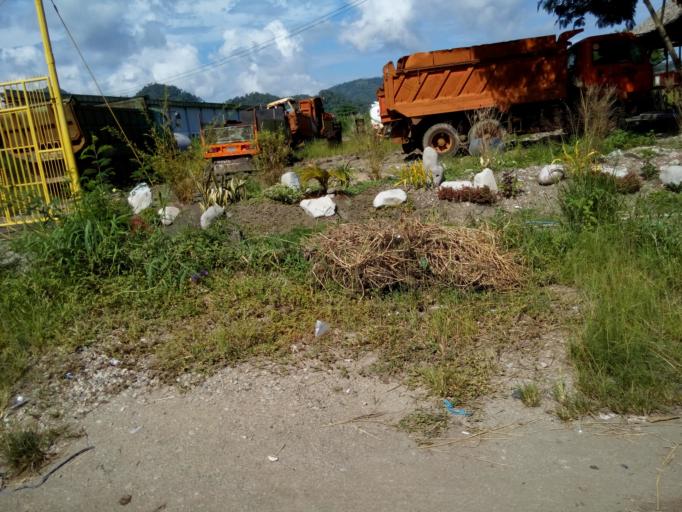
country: PH
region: Caraga
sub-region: Province of Surigao del Norte
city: Luna
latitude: 9.7588
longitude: 125.4828
